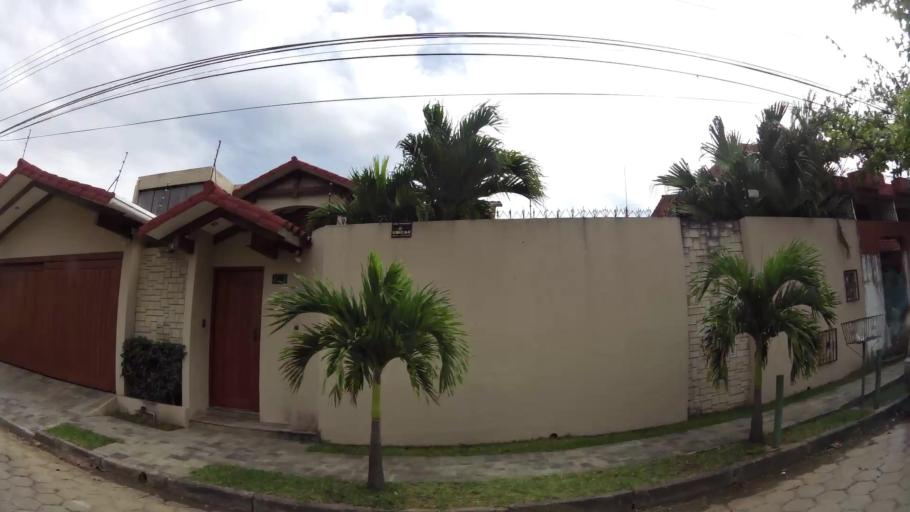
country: BO
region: Santa Cruz
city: Santa Cruz de la Sierra
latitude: -17.7962
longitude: -63.2005
